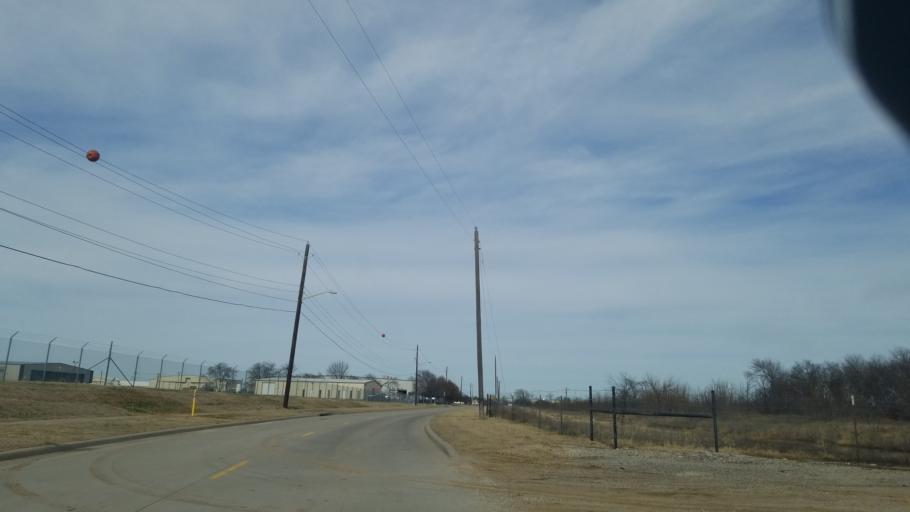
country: US
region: Texas
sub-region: Denton County
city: Denton
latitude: 33.1981
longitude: -97.1906
